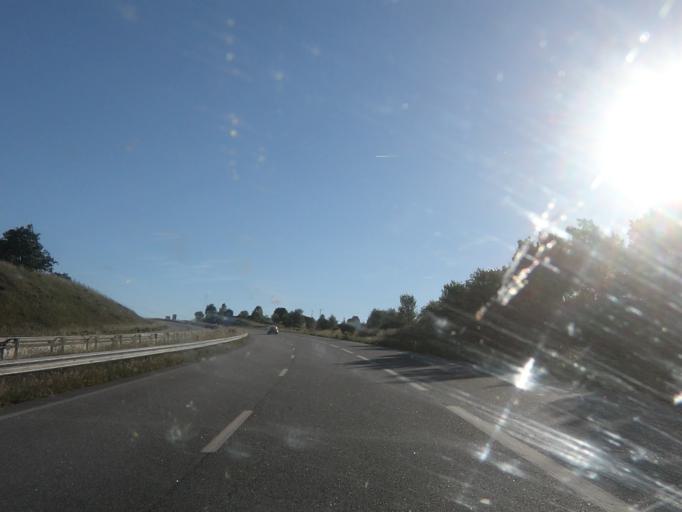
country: ES
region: Castille and Leon
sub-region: Provincia de Salamanca
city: Fuentes de Onoro
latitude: 40.6071
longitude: -6.9388
